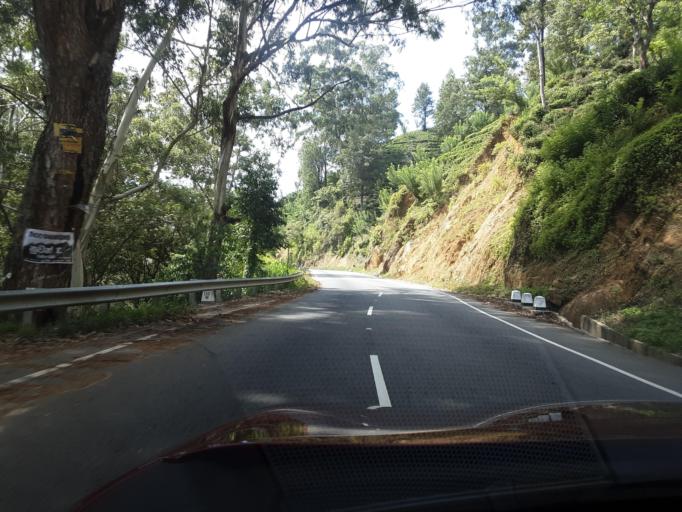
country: LK
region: Uva
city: Badulla
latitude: 6.9602
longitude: 81.1137
